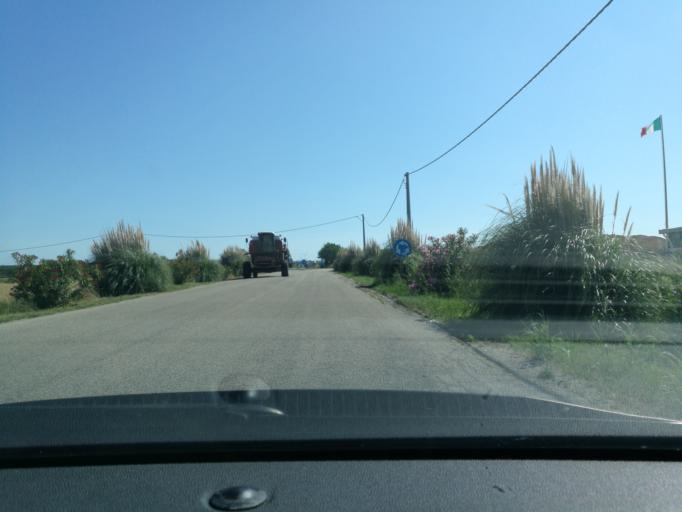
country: IT
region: Abruzzo
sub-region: Provincia di Chieti
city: Vasto
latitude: 42.1707
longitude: 14.6961
